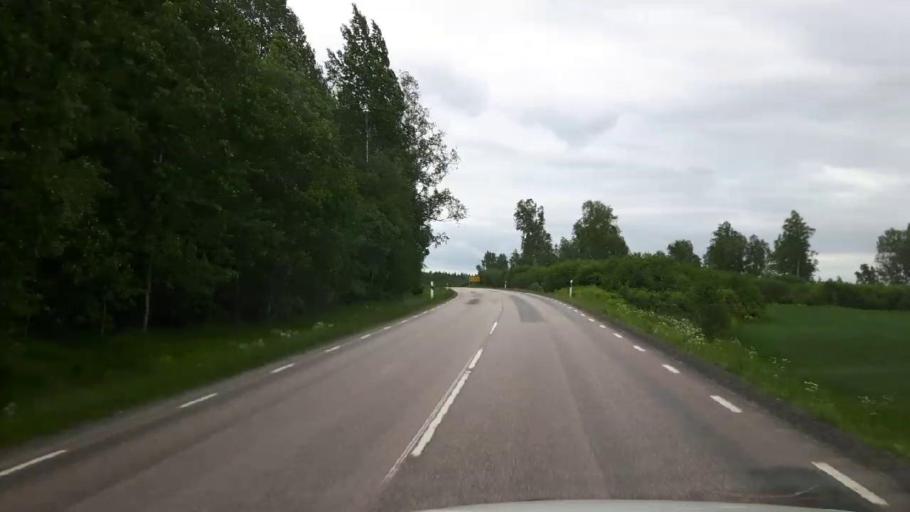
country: SE
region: Vaestmanland
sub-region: Kopings Kommun
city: Kolsva
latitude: 59.6183
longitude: 15.8216
